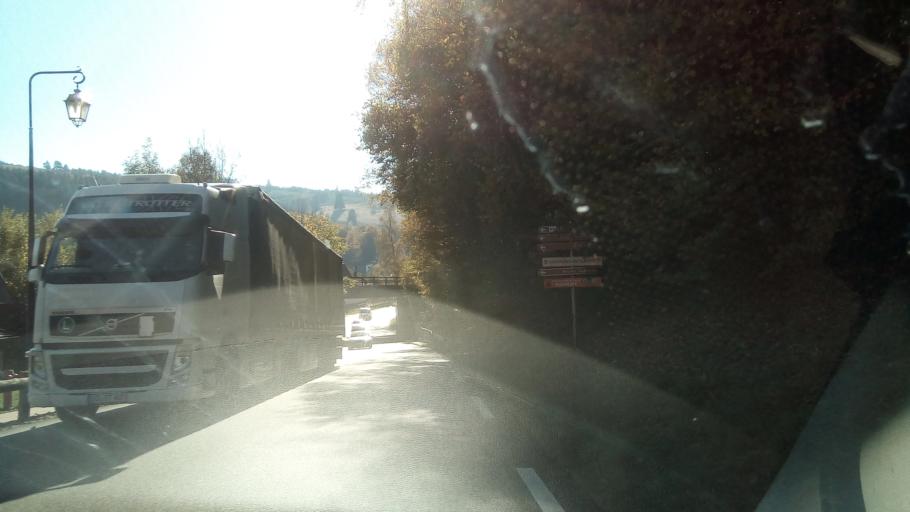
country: FR
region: Alsace
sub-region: Departement du Bas-Rhin
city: Rothau
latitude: 48.4291
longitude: 7.1833
